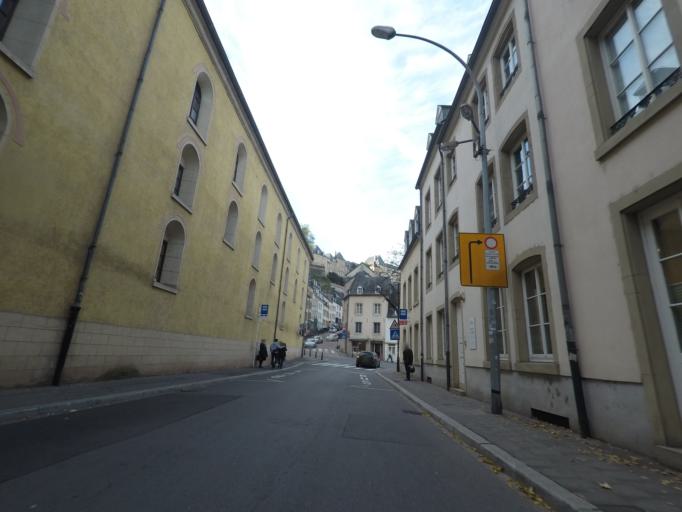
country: LU
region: Luxembourg
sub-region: Canton de Luxembourg
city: Luxembourg
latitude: 49.5950
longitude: 6.1481
